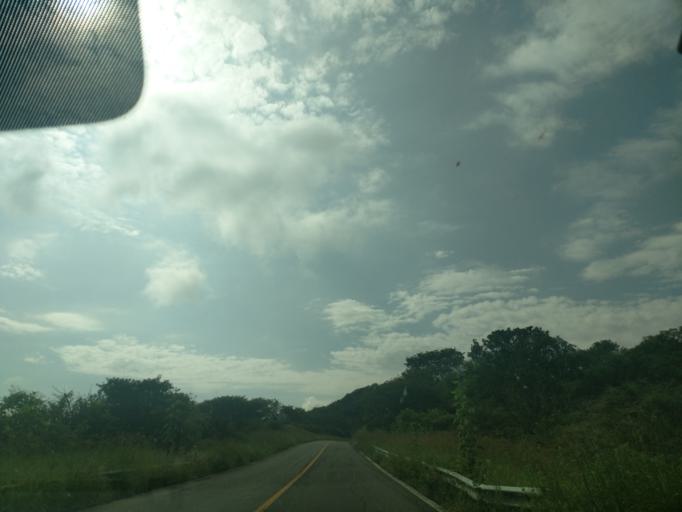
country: MX
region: Jalisco
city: El Salto
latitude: 20.3955
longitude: -104.5260
